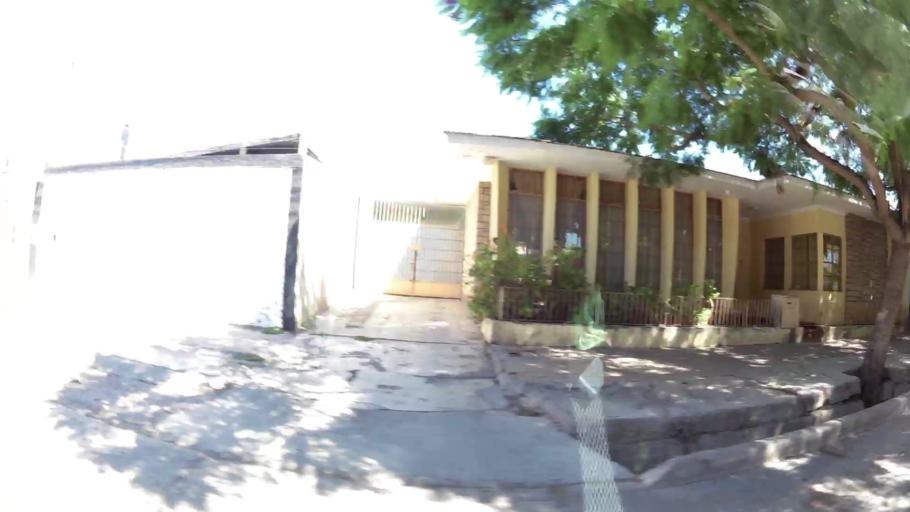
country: AR
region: Mendoza
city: Las Heras
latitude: -32.8468
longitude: -68.8417
